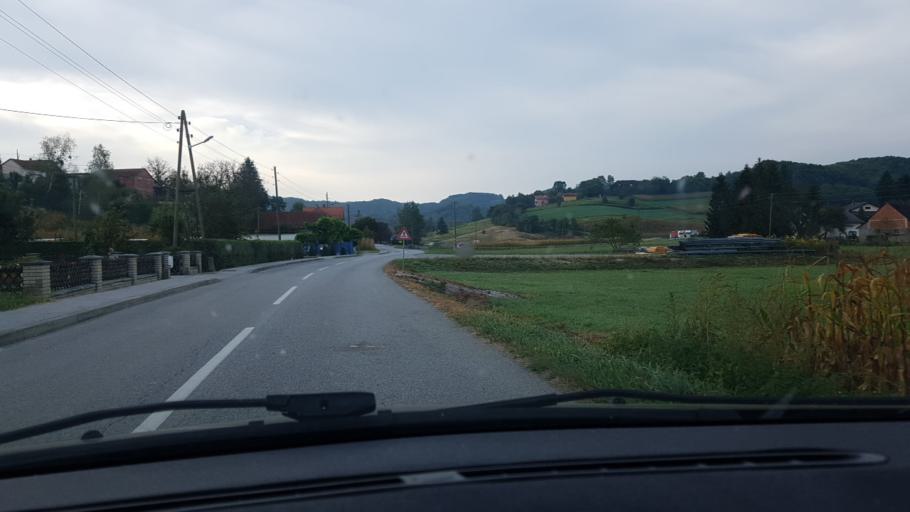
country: HR
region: Krapinsko-Zagorska
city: Mihovljan
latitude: 46.1389
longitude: 15.9649
